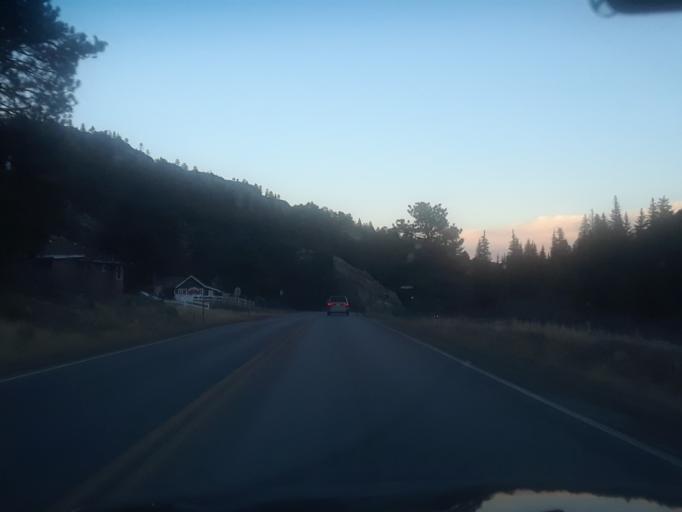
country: US
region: Colorado
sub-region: Jefferson County
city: Evergreen
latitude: 39.4131
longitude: -105.5149
